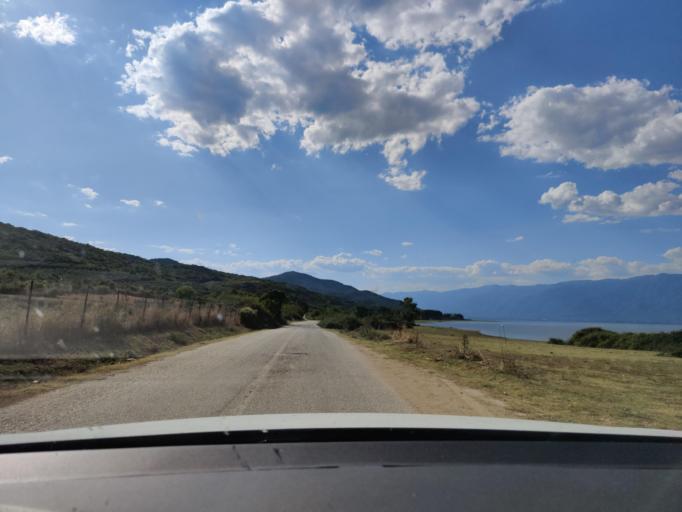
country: GR
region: Central Macedonia
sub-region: Nomos Serron
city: Chrysochorafa
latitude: 41.1526
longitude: 23.2020
